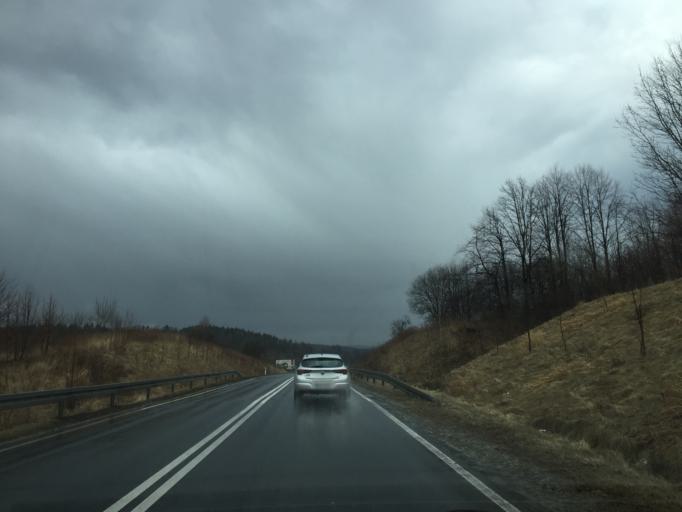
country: PL
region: Lesser Poland Voivodeship
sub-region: Powiat suski
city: Zembrzyce
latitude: 49.7711
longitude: 19.6060
